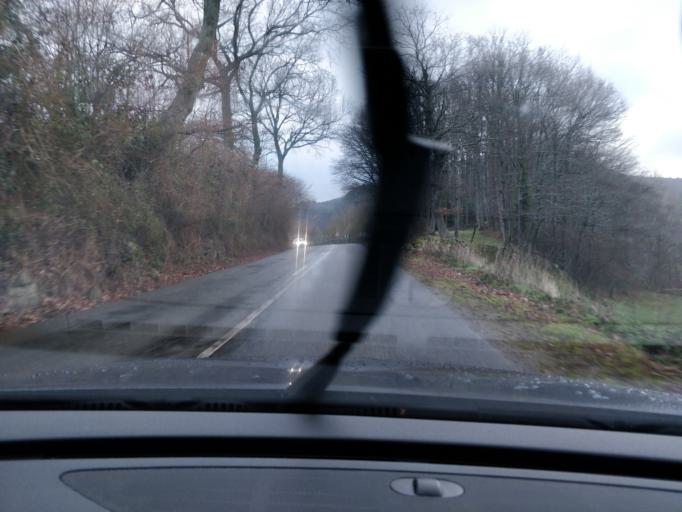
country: ES
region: Castille and Leon
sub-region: Provincia de Burgos
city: Espinosa de los Monteros
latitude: 43.1036
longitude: -3.5717
